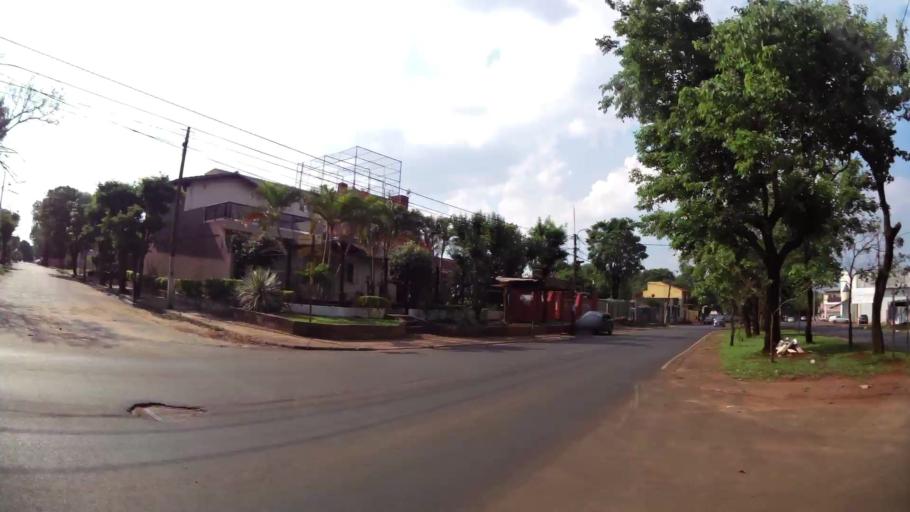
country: PY
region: Alto Parana
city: Presidente Franco
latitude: -25.5304
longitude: -54.6235
